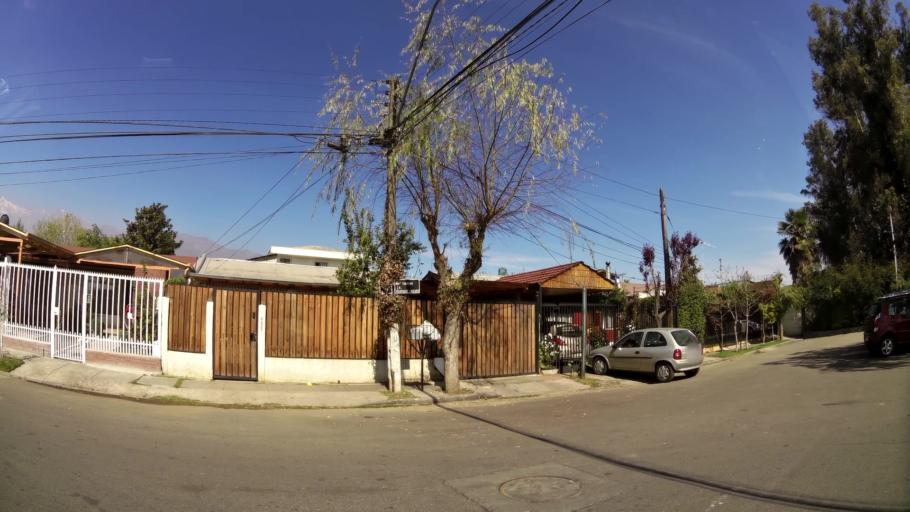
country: CL
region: Santiago Metropolitan
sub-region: Provincia de Santiago
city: Villa Presidente Frei, Nunoa, Santiago, Chile
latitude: -33.4996
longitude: -70.5824
